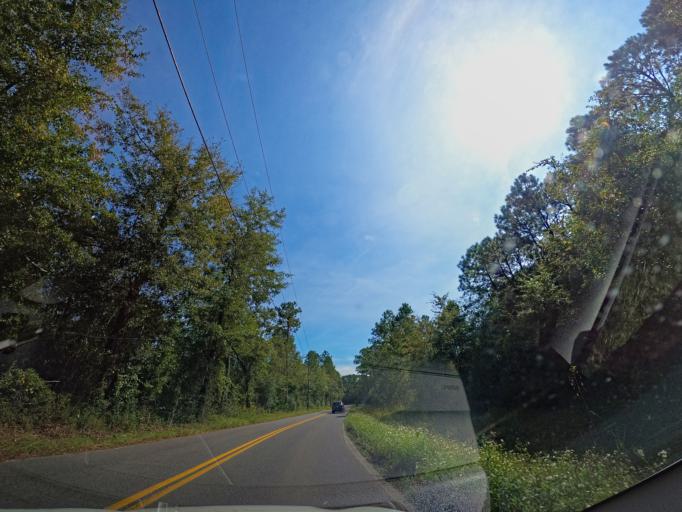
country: US
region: Florida
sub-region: Okaloosa County
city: Crestview
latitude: 30.7026
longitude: -86.5799
